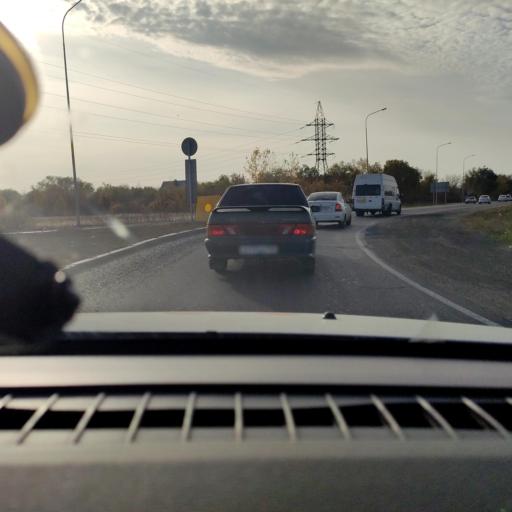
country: RU
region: Samara
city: Samara
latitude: 53.1323
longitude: 50.1375
